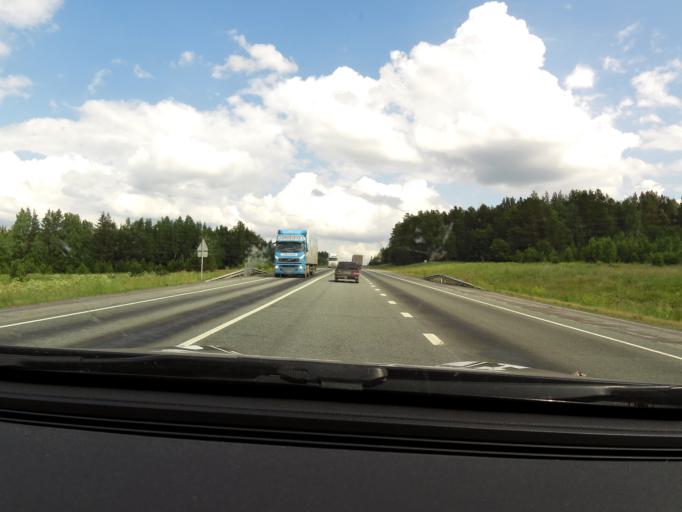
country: RU
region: Sverdlovsk
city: Bisert'
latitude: 56.7967
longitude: 58.6678
